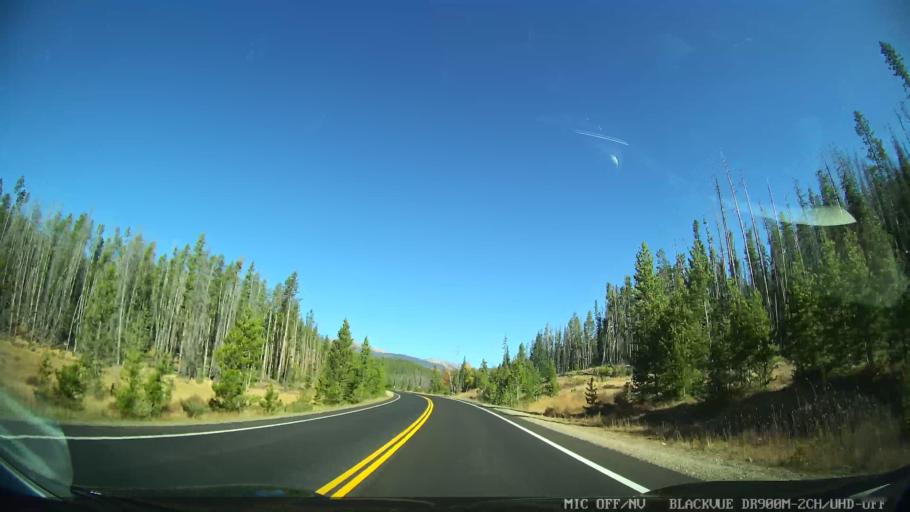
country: US
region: Colorado
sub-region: Grand County
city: Granby
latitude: 40.3143
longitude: -105.8431
